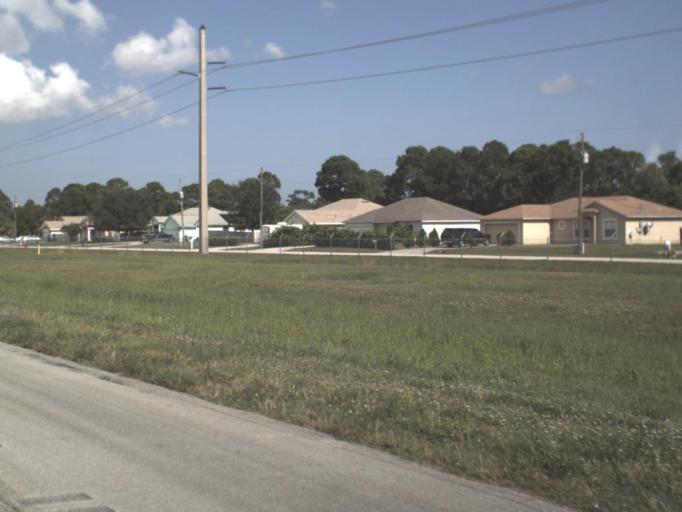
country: US
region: Florida
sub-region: Saint Lucie County
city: River Park
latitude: 27.3315
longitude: -80.3742
